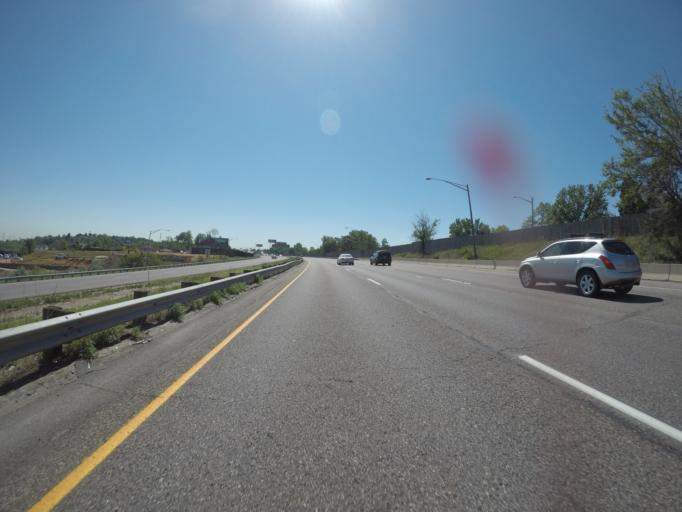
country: US
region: Colorado
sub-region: Jefferson County
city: Wheat Ridge
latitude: 39.7840
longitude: -105.0701
